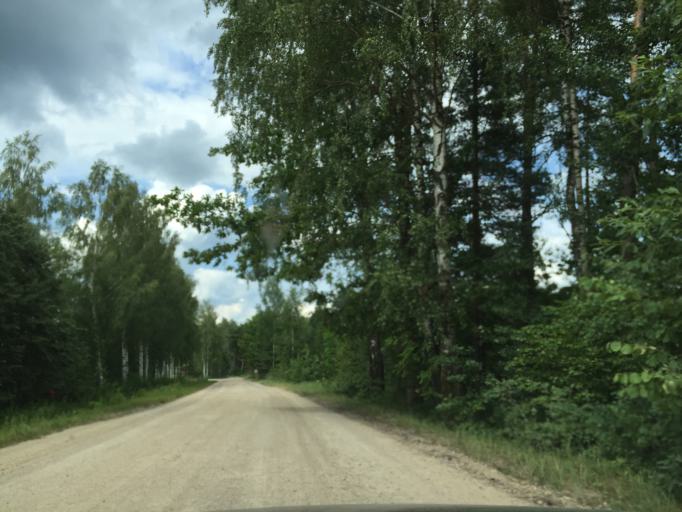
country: LV
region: Jelgava
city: Jelgava
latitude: 56.6336
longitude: 23.6239
